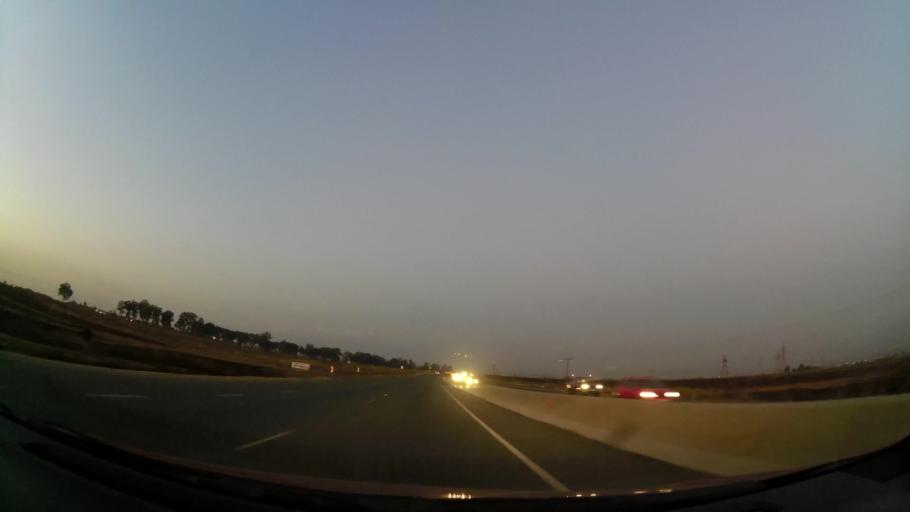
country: ZA
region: Gauteng
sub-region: City of Johannesburg Metropolitan Municipality
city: Soweto
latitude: -26.2963
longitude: 27.8267
